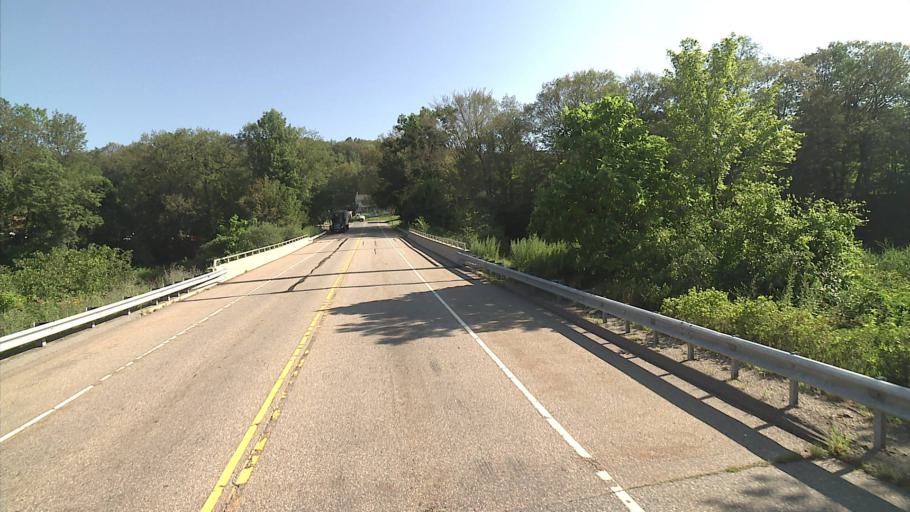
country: US
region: Connecticut
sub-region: New London County
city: Montville Center
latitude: 41.5636
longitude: -72.1647
